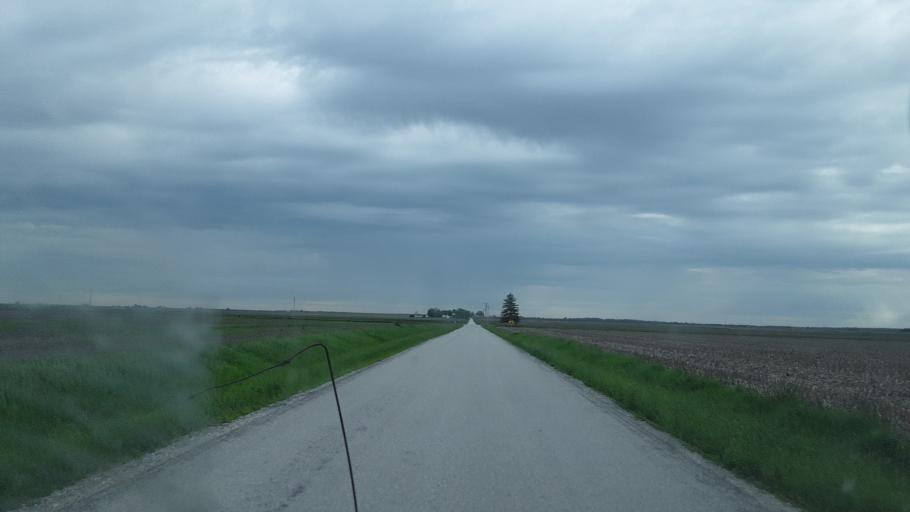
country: US
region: Illinois
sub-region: McDonough County
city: Bushnell
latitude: 40.3807
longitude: -90.5106
